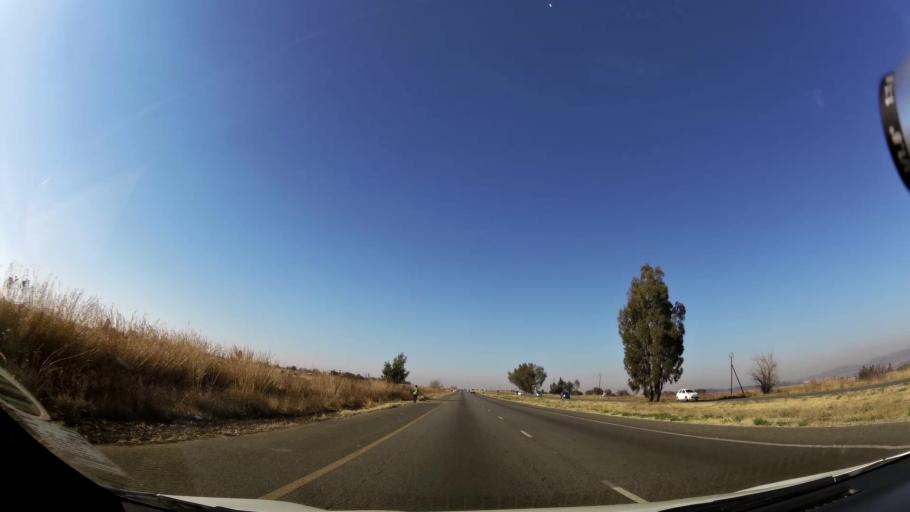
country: ZA
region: Gauteng
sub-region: City of Johannesburg Metropolitan Municipality
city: Johannesburg
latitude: -26.3195
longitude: 28.0650
